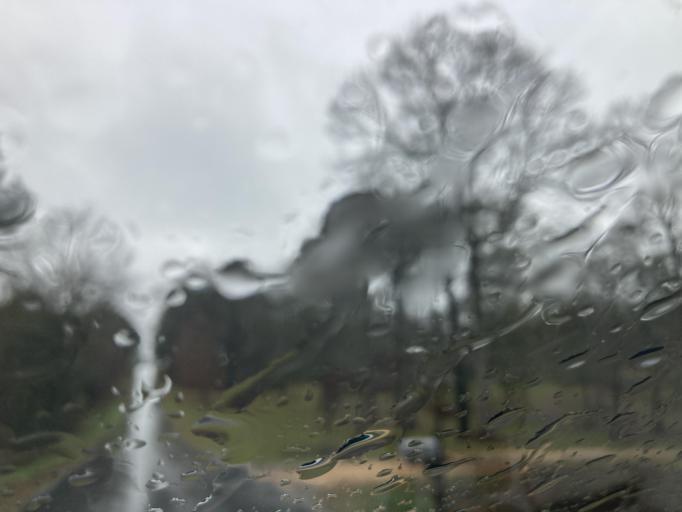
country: US
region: Mississippi
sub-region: Forrest County
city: Rawls Springs
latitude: 31.4814
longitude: -89.3835
